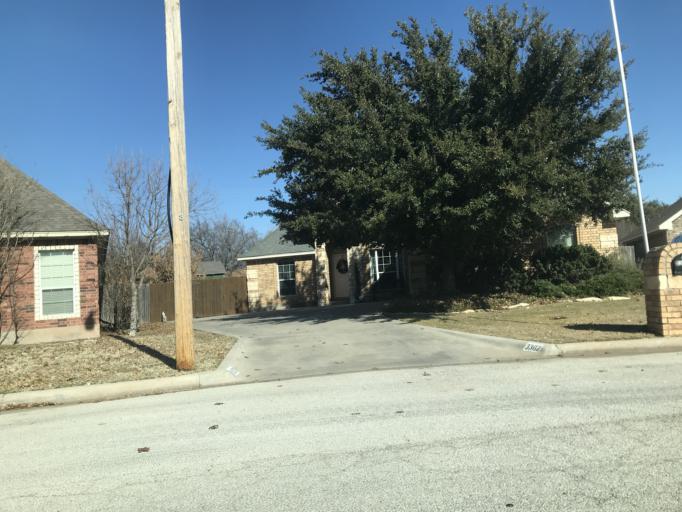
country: US
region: Texas
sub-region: Taylor County
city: Abilene
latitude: 32.3819
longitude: -99.7644
